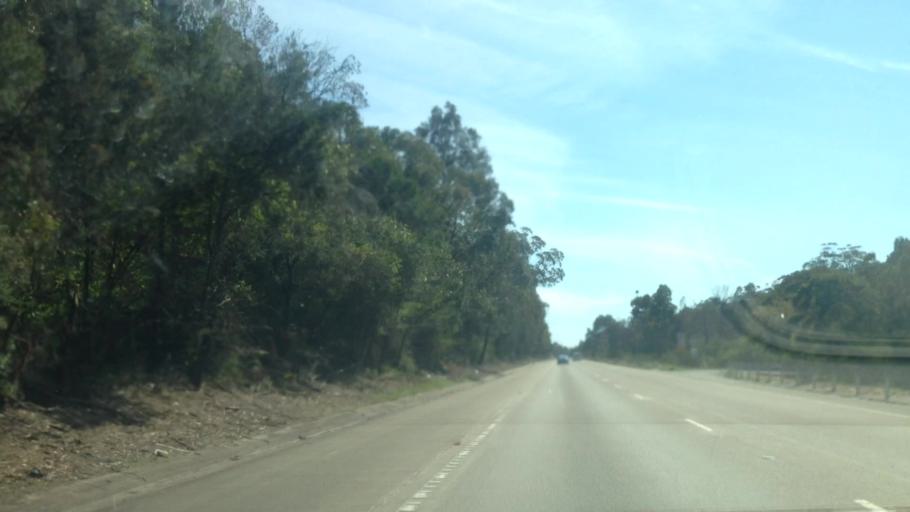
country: AU
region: New South Wales
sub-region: Lake Macquarie Shire
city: Fennell Bay
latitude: -32.9697
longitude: 151.5345
